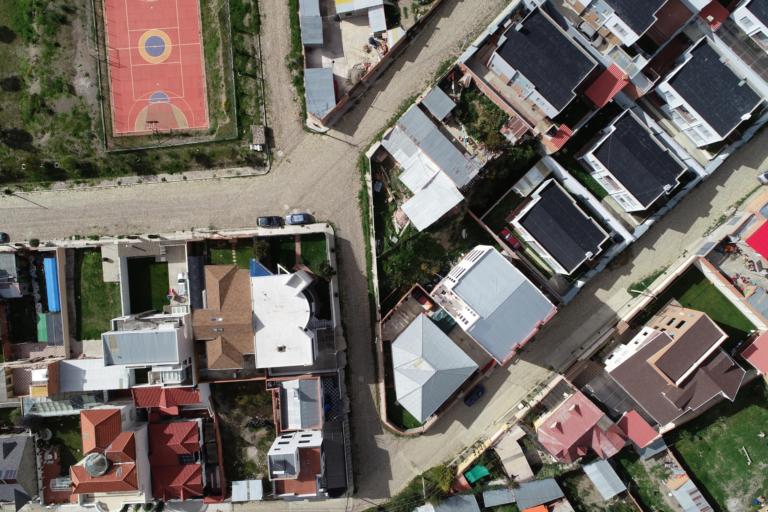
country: BO
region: La Paz
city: La Paz
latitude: -16.5016
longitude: -68.0757
